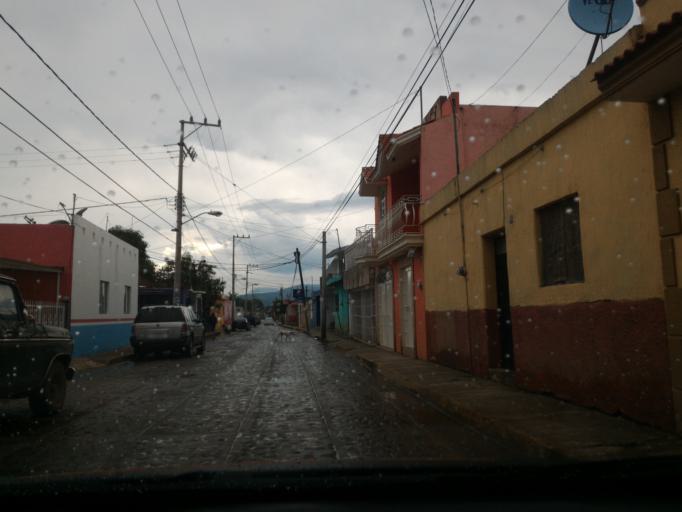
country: MX
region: Jalisco
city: San Andres Ixtlan
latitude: 19.8204
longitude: -103.4693
